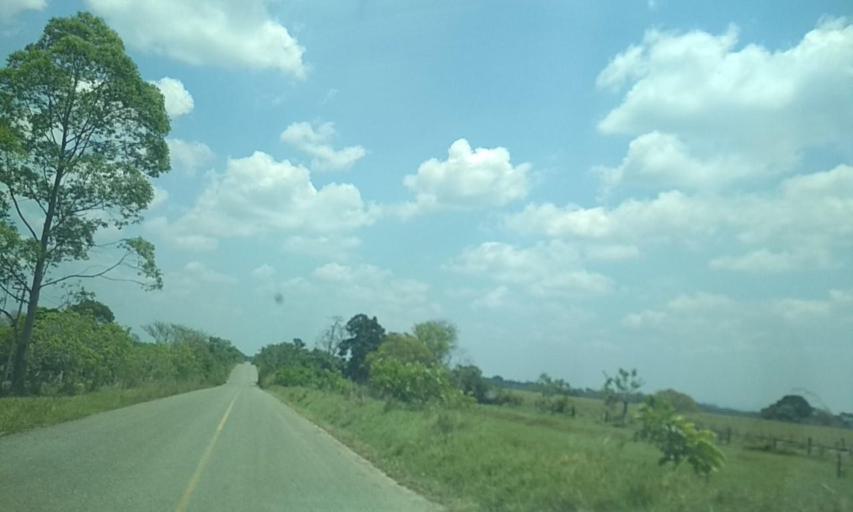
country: MX
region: Tabasco
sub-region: Huimanguillo
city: Francisco Rueda
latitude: 17.8036
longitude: -93.8611
